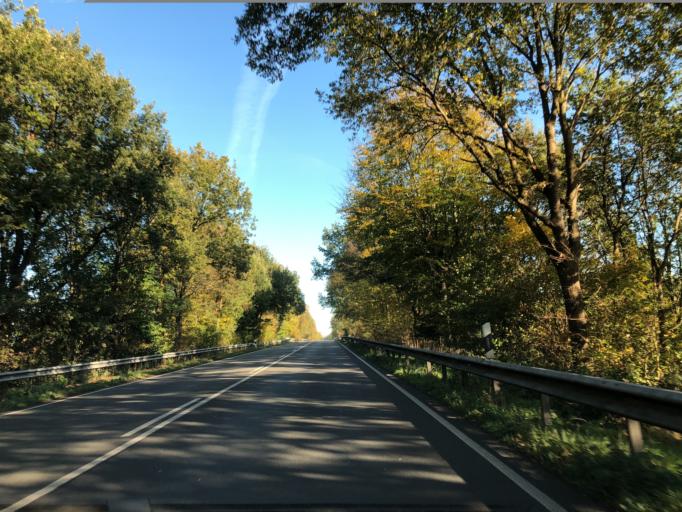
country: DE
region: Lower Saxony
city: Lehe
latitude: 53.0425
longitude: 7.3311
